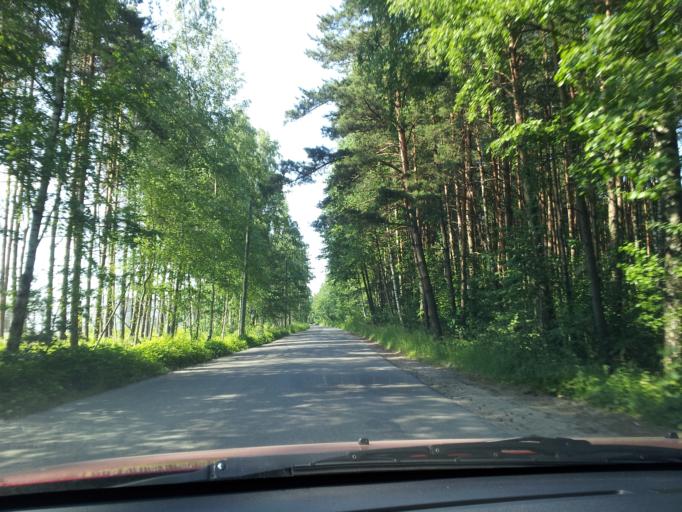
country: LV
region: Riga
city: Bolderaja
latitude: 57.0575
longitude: 24.0592
